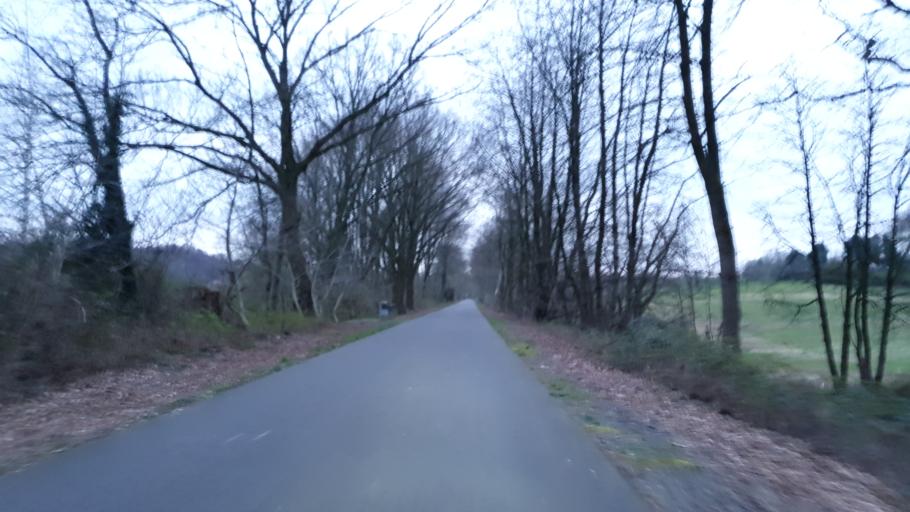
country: DE
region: North Rhine-Westphalia
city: Leichlingen
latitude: 51.0846
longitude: 7.0479
